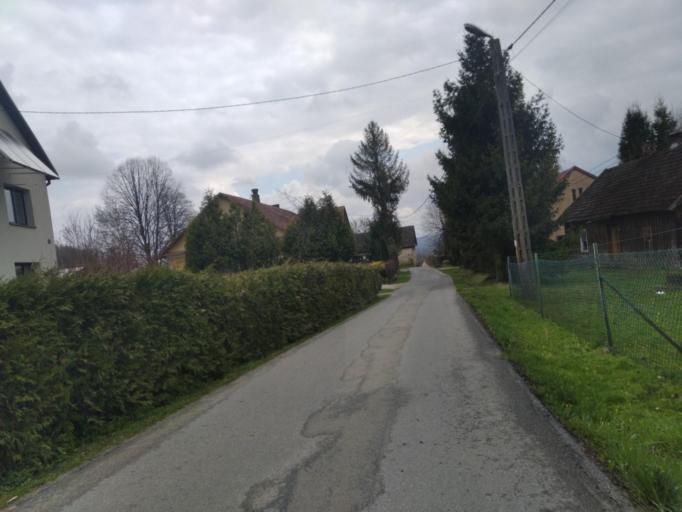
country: PL
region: Subcarpathian Voivodeship
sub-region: Powiat strzyzowski
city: Wisniowa
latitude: 49.8779
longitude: 21.6933
